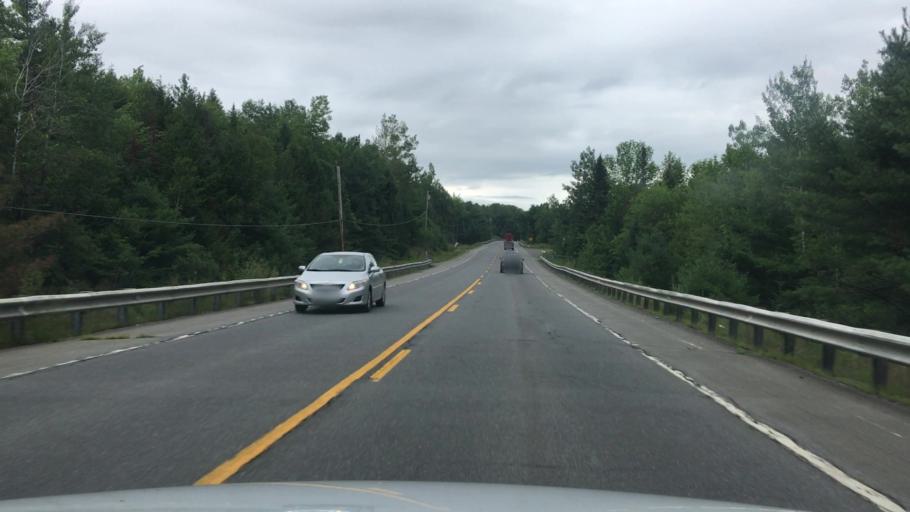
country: US
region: Maine
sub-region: Penobscot County
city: Bradley
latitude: 44.8253
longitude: -68.3971
